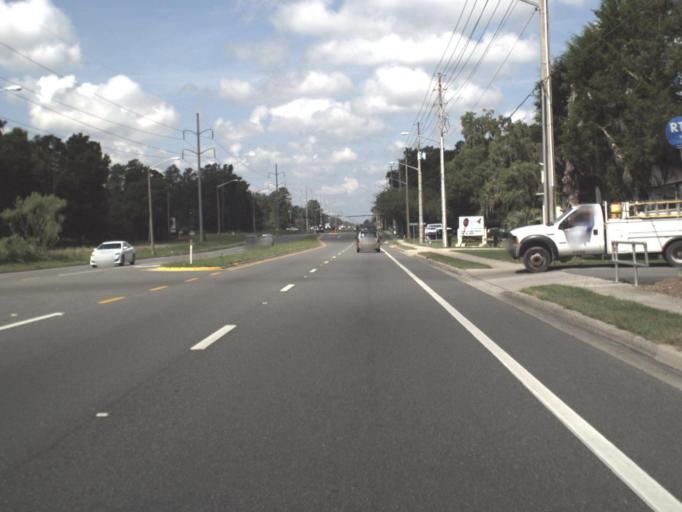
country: US
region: Florida
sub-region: Alachua County
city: Gainesville
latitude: 29.6074
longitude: -82.4054
